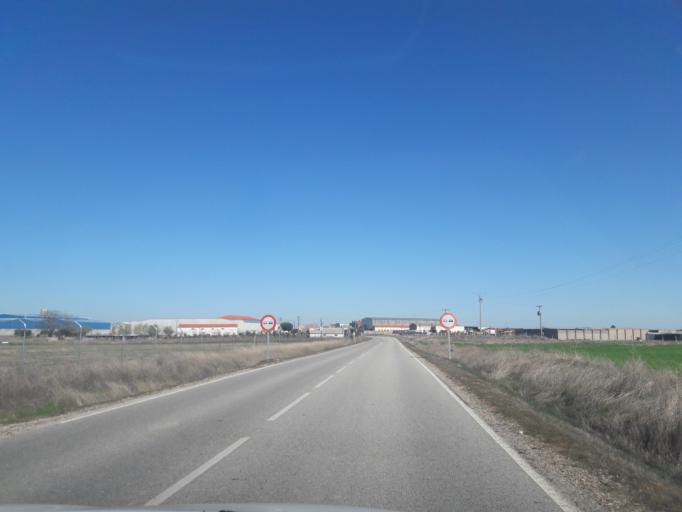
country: ES
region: Castille and Leon
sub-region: Provincia de Salamanca
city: Penaranda de Bracamonte
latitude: 40.8885
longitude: -5.1971
